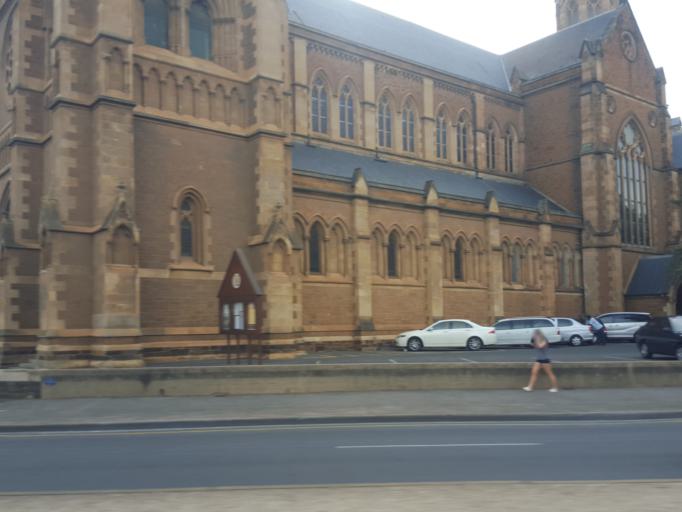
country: AU
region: South Australia
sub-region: Adelaide
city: North Adelaide
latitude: -34.9128
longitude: 138.5987
